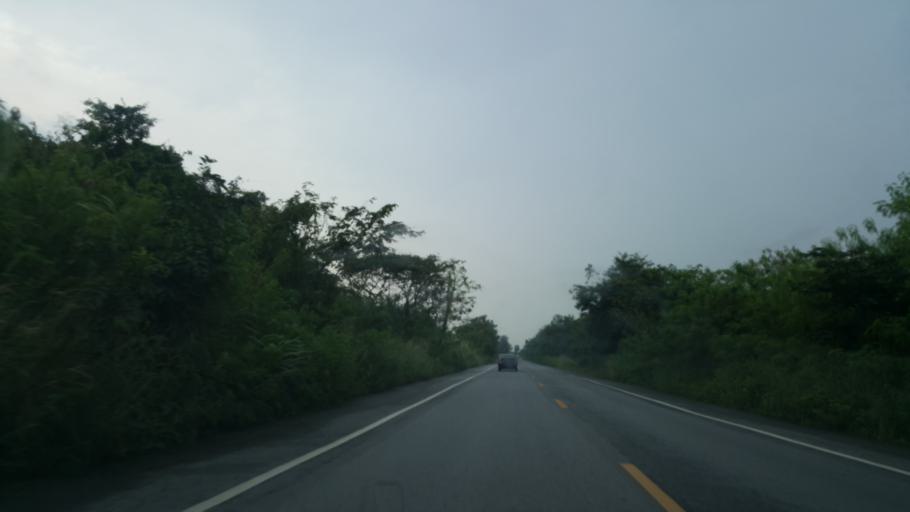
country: TH
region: Chon Buri
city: Sattahip
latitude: 12.7295
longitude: 100.9565
